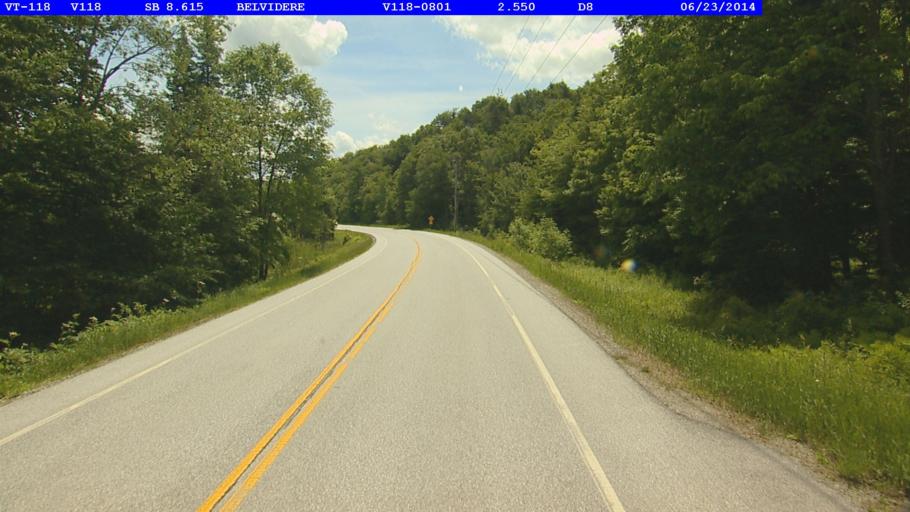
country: US
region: Vermont
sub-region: Lamoille County
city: Johnson
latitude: 44.7955
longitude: -72.6240
